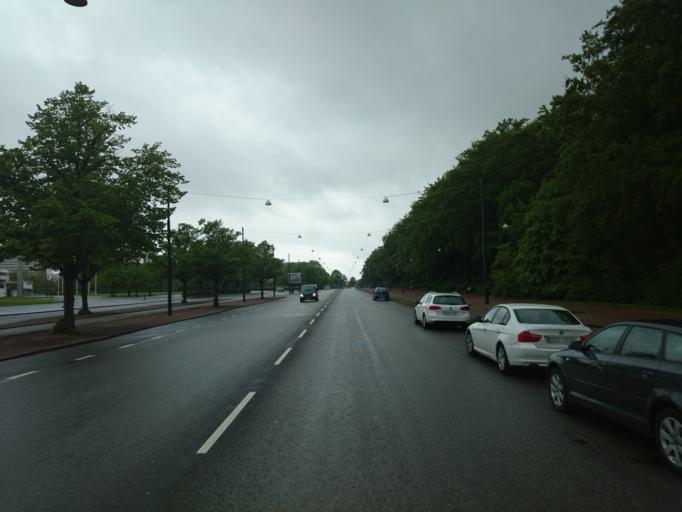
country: SE
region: Skane
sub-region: Malmo
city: Malmoe
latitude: 55.5872
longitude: 12.9922
